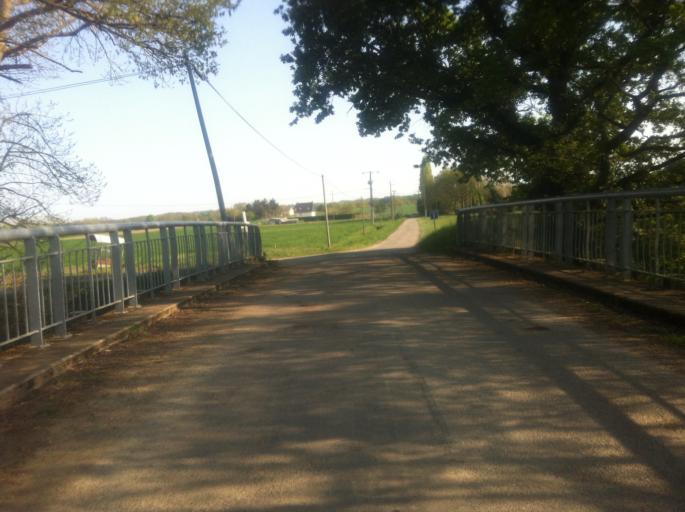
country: FR
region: Brittany
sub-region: Departement d'Ille-et-Vilaine
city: Bruz
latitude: 48.0160
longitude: -1.7281
